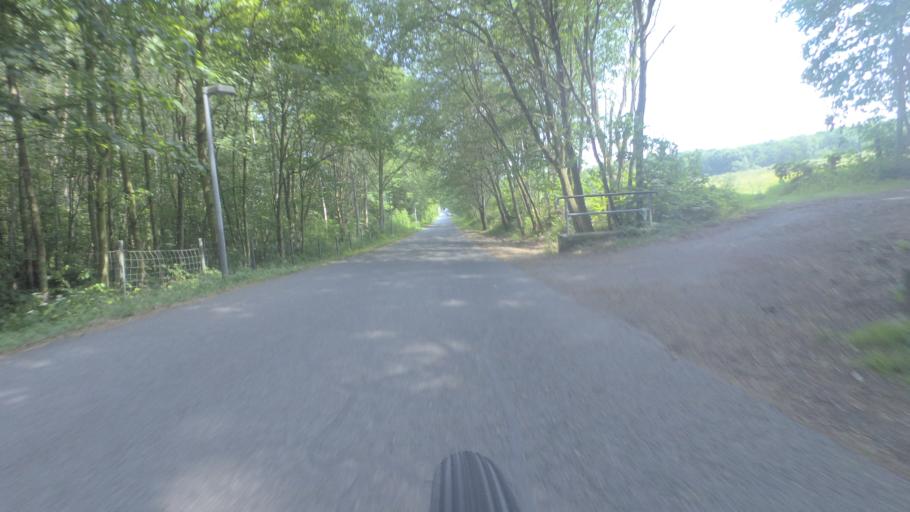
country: DE
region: Saxony-Anhalt
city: Ballenstedt
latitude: 51.7120
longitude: 11.2407
